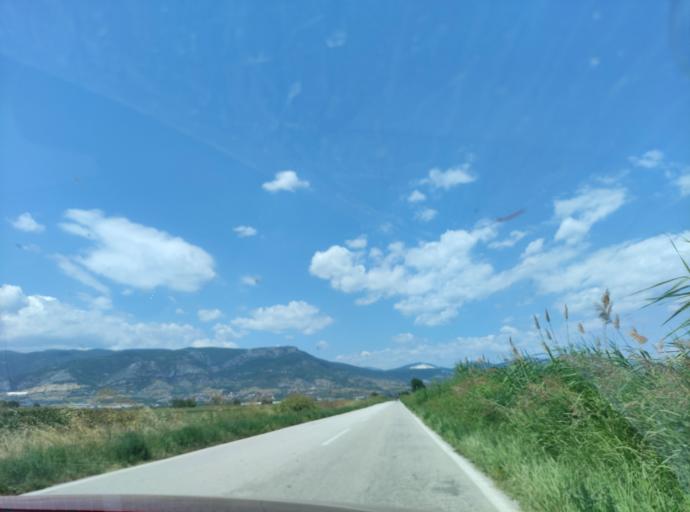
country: GR
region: East Macedonia and Thrace
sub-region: Nomos Kavalas
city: Chrysoupolis
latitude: 40.9580
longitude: 24.6273
